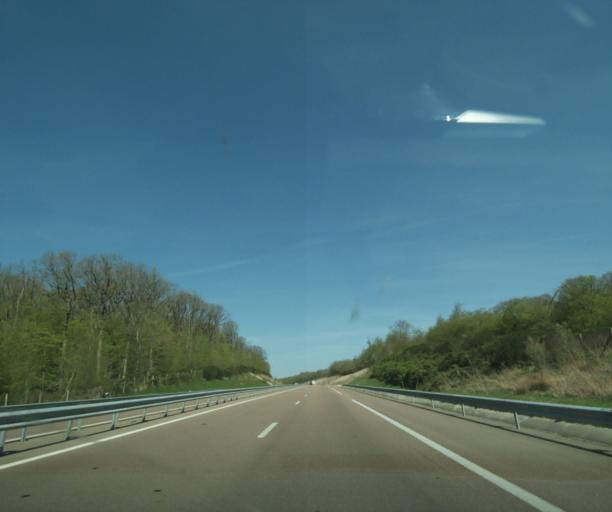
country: FR
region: Bourgogne
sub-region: Departement de la Nievre
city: Challuy
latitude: 46.9172
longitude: 3.1616
